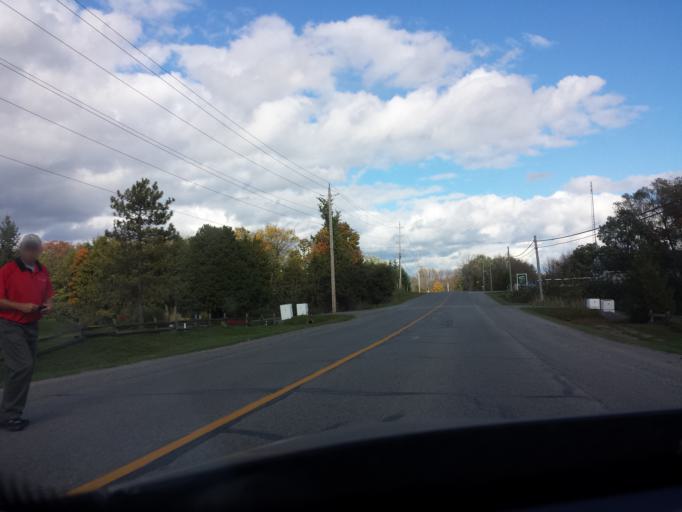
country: CA
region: Ontario
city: Carleton Place
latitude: 45.1727
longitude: -76.1275
